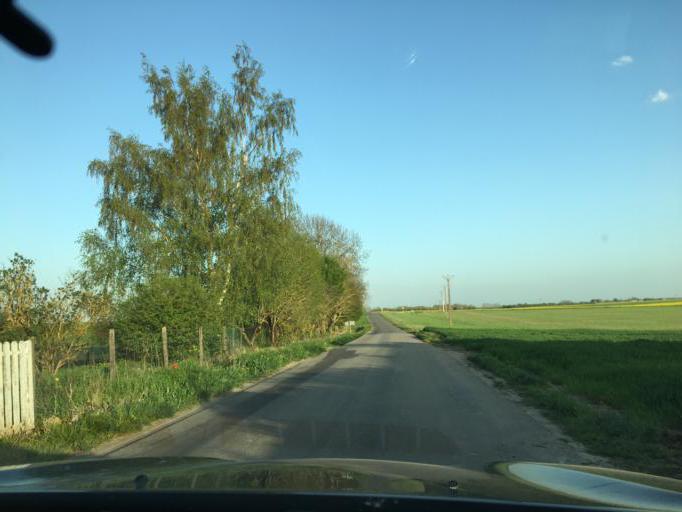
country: FR
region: Centre
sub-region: Departement du Loiret
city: Tavers
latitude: 47.8045
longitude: 1.5347
